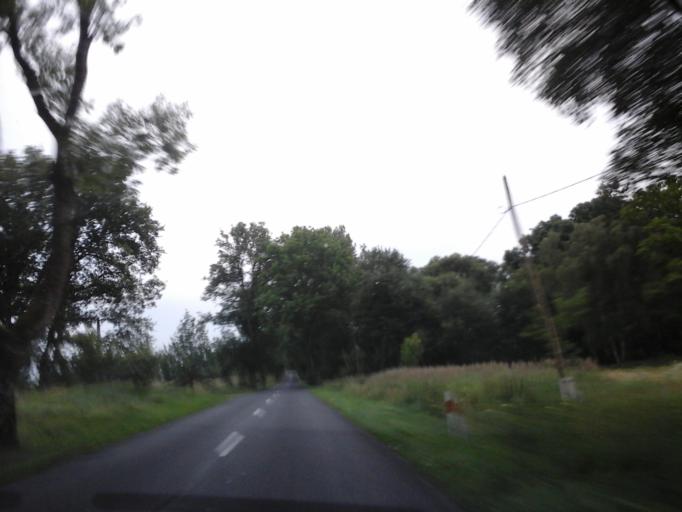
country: PL
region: West Pomeranian Voivodeship
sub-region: Powiat goleniowski
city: Maszewo
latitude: 53.5565
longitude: 15.1275
